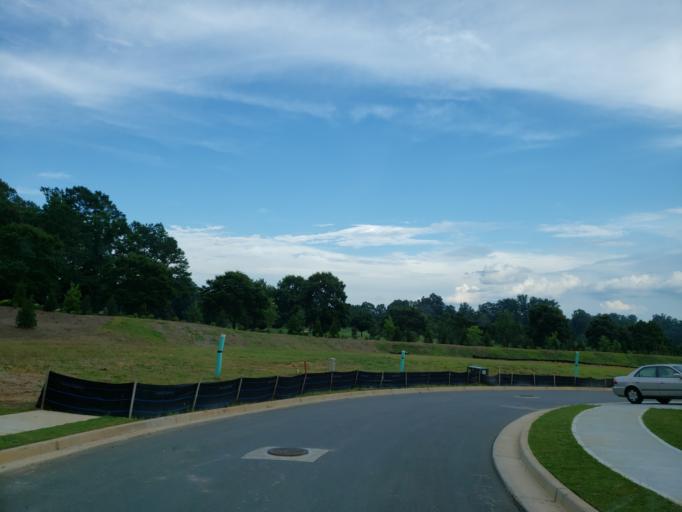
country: US
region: Georgia
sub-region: Cherokee County
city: Ball Ground
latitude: 34.2317
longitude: -84.3565
